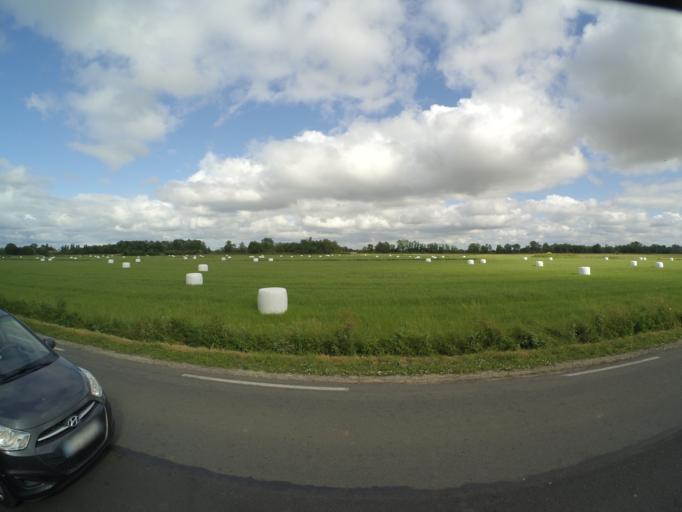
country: FR
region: Aquitaine
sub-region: Departement de la Gironde
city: Saint-Louis-de-Montferrand
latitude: 44.9461
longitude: -0.5585
